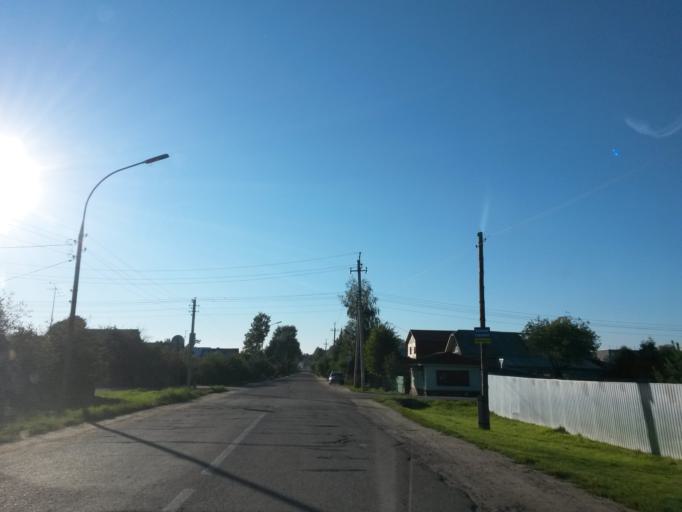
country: RU
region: Jaroslavl
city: Gavrilov-Yam
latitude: 57.2965
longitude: 39.8731
